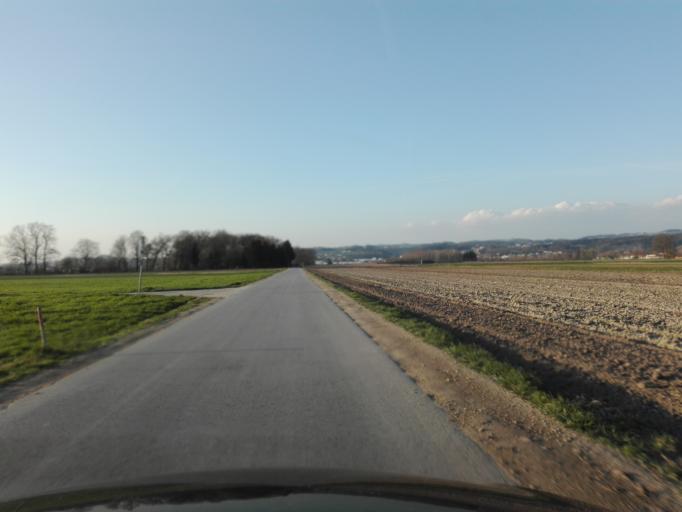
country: AT
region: Upper Austria
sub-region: Politischer Bezirk Perg
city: Perg
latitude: 48.2247
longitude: 14.6420
